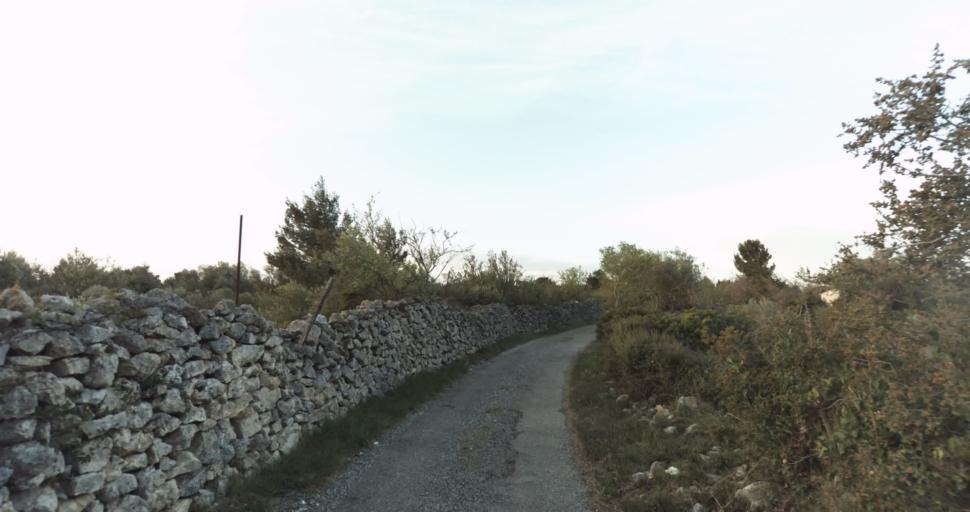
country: FR
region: Languedoc-Roussillon
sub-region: Departement de l'Aude
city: Leucate
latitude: 42.9268
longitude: 3.0214
